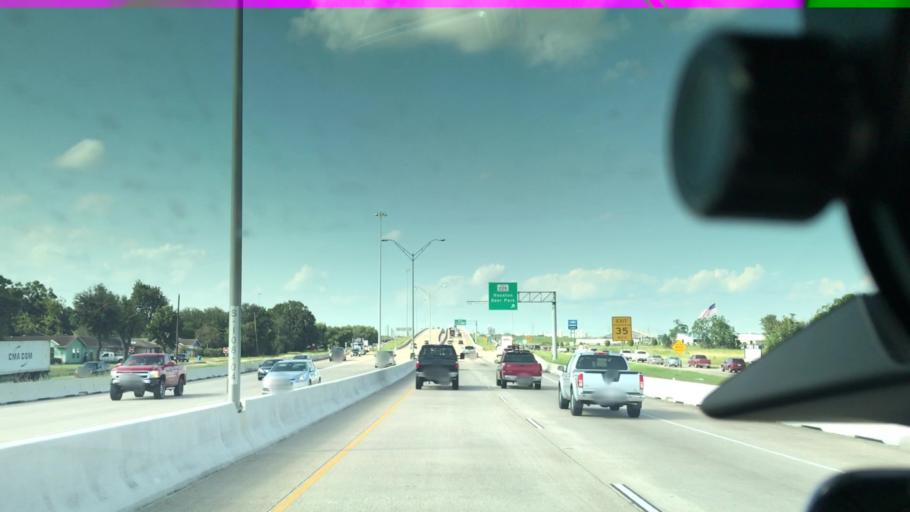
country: US
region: Texas
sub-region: Harris County
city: Deer Park
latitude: 29.7046
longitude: -95.1534
